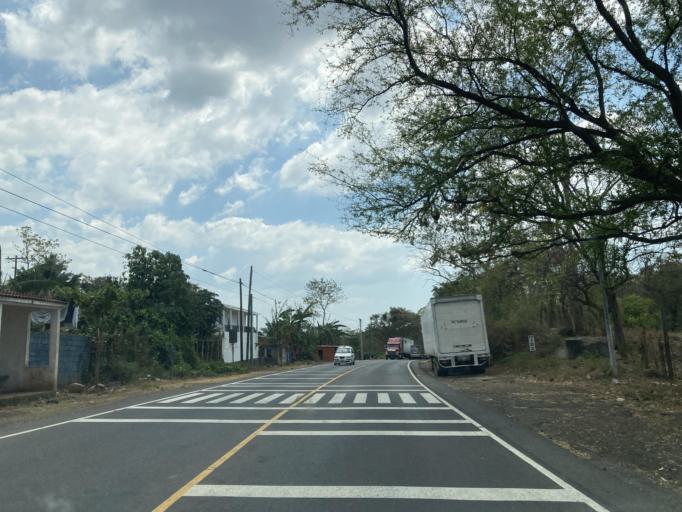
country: GT
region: Santa Rosa
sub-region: Municipio de Taxisco
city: Taxisco
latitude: 14.0887
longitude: -90.4968
